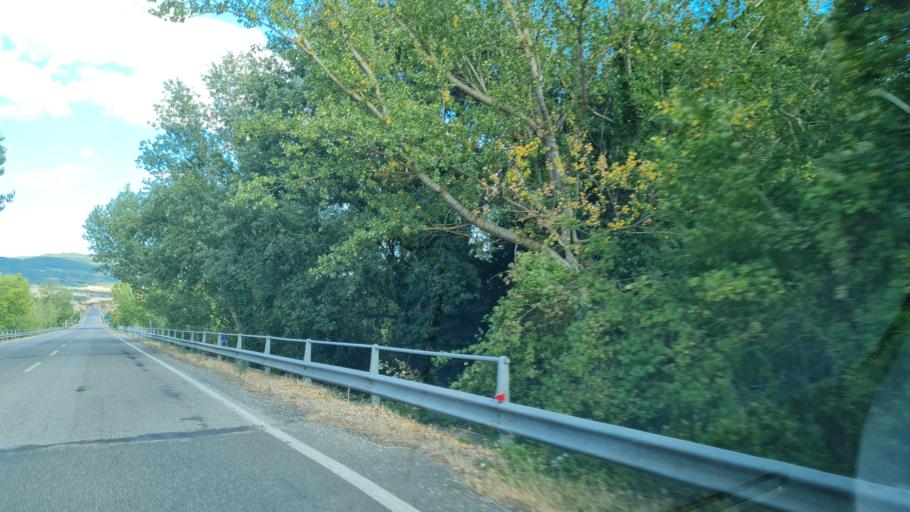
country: IT
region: Tuscany
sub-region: Provincia di Siena
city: Chianciano Terme
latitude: 43.0073
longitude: 11.7380
